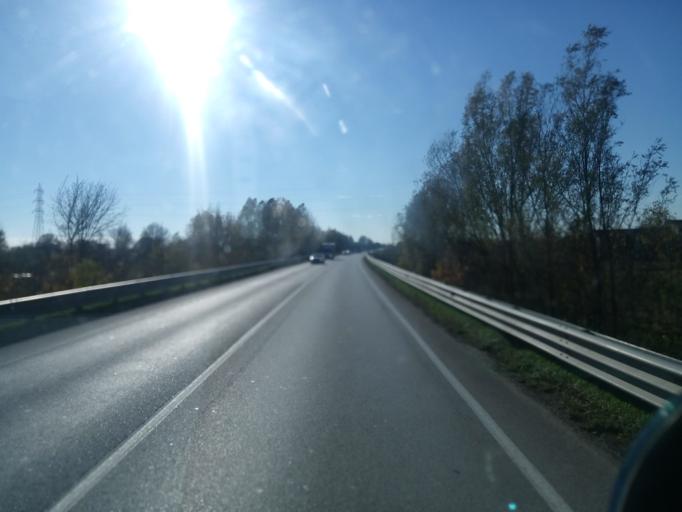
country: IT
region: Veneto
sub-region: Provincia di Padova
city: Loreggia
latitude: 45.5785
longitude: 11.9569
